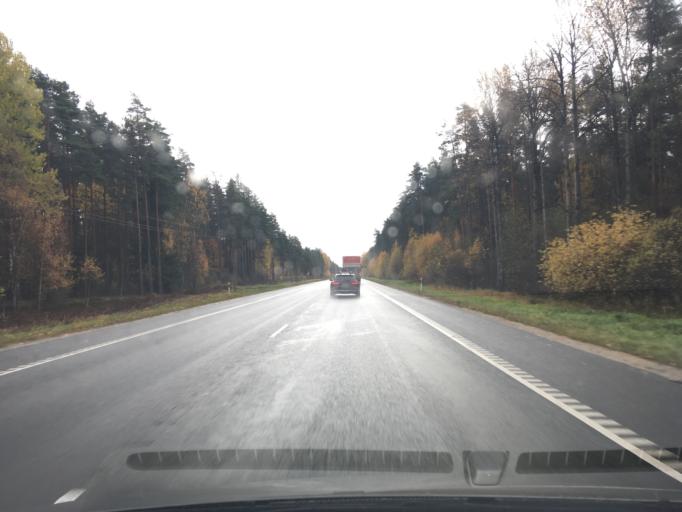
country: EE
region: Tartu
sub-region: Tartu linn
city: Tartu
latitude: 58.3974
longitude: 26.6603
